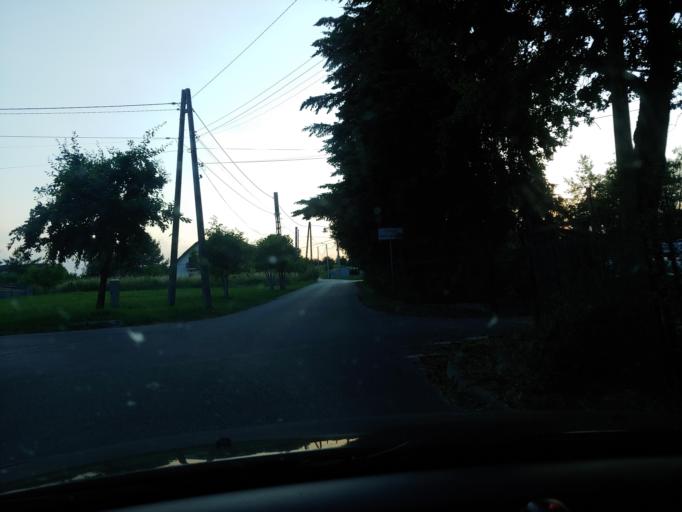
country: PL
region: Lesser Poland Voivodeship
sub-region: Powiat chrzanowski
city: Trzebinia
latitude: 50.1713
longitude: 19.4710
